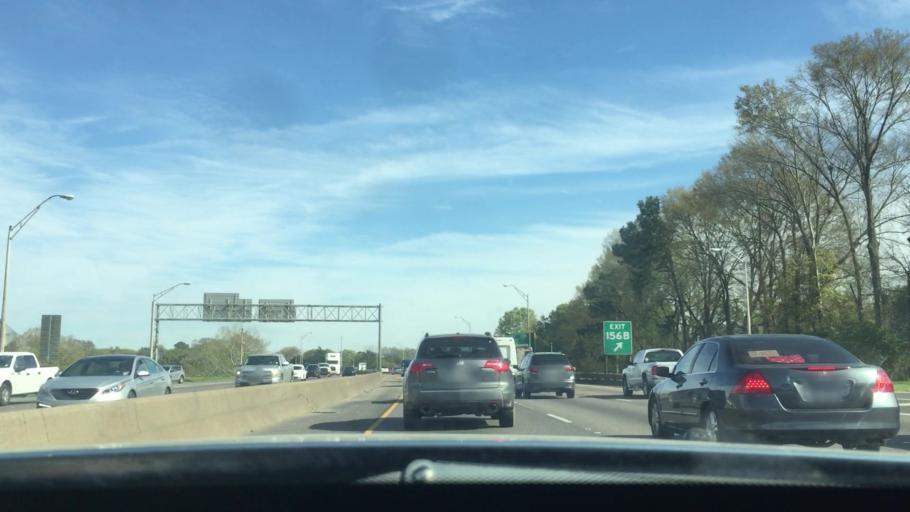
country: US
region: Louisiana
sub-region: East Baton Rouge Parish
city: Baton Rouge
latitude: 30.4281
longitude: -91.1707
